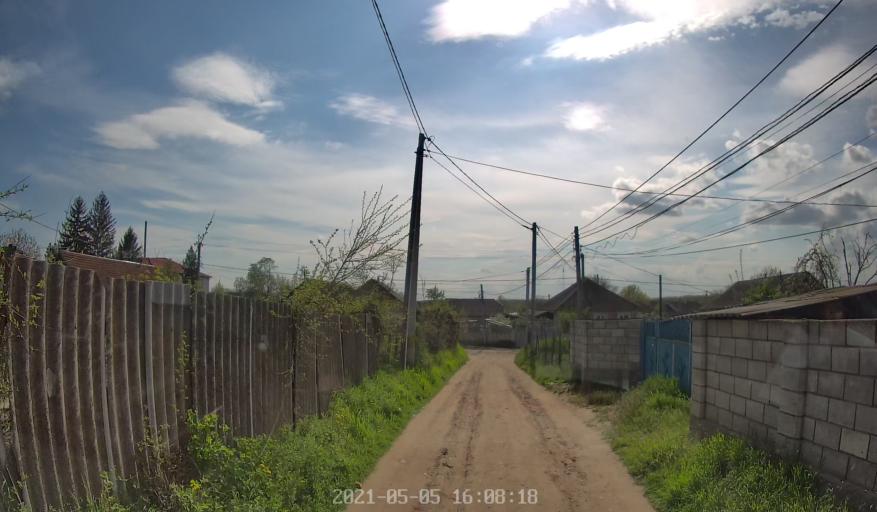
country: MD
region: Criuleni
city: Criuleni
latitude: 47.1418
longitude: 29.1984
